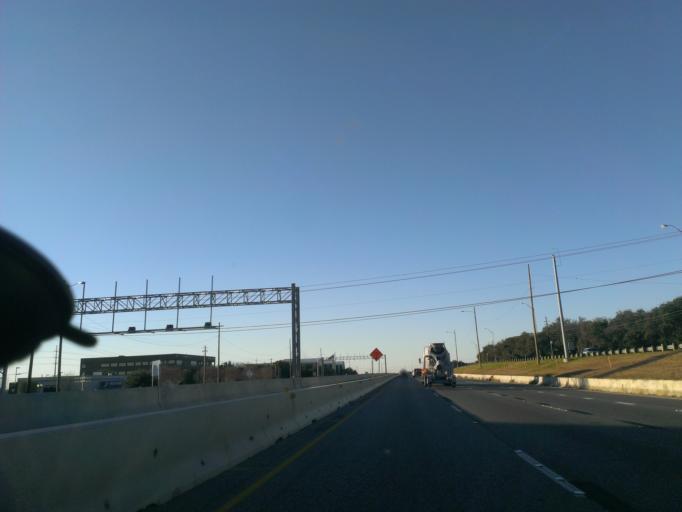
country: US
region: Texas
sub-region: Williamson County
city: Jollyville
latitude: 30.3743
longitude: -97.7403
